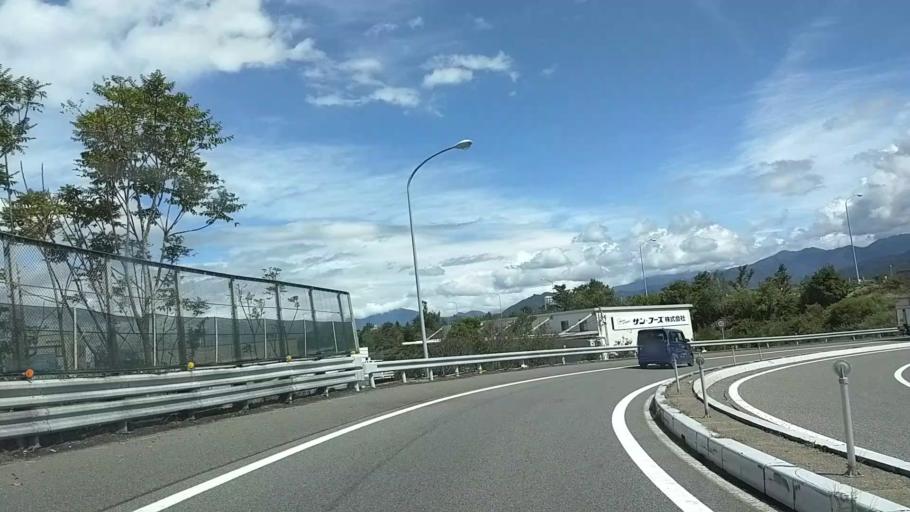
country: JP
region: Nagano
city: Suzaka
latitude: 36.6344
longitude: 138.2720
